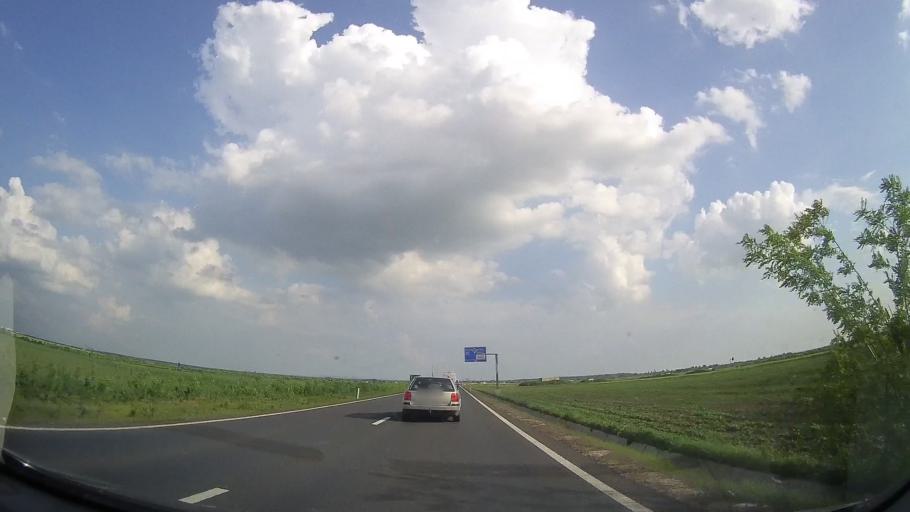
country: RO
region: Timis
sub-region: Comuna Remetea Mare
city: Remetea Mare
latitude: 45.7982
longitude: 21.4131
